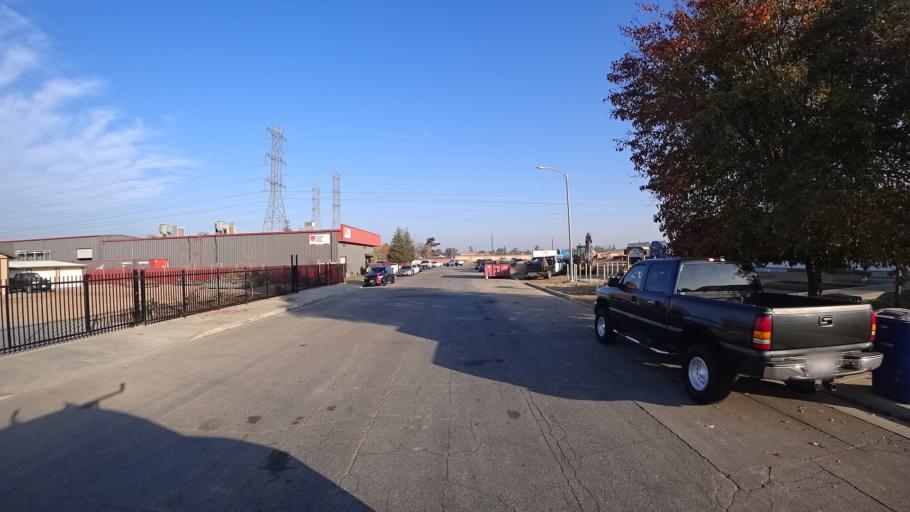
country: US
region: California
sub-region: Kern County
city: Greenacres
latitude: 35.3858
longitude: -119.1144
